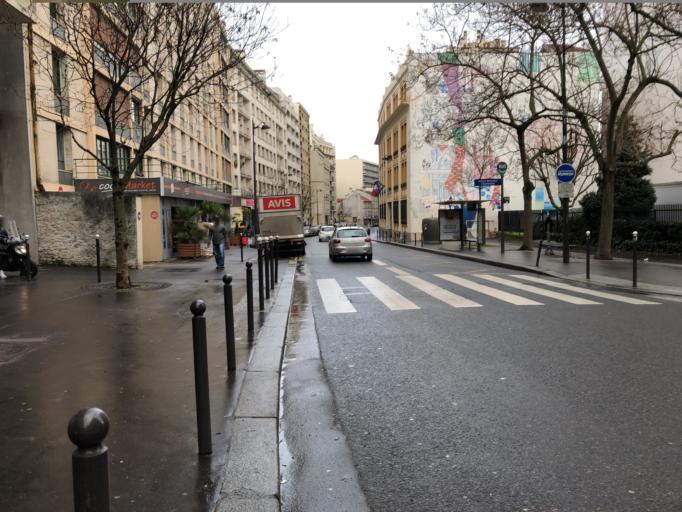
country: FR
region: Ile-de-France
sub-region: Departement du Val-de-Marne
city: Gentilly
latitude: 48.8220
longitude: 2.3421
